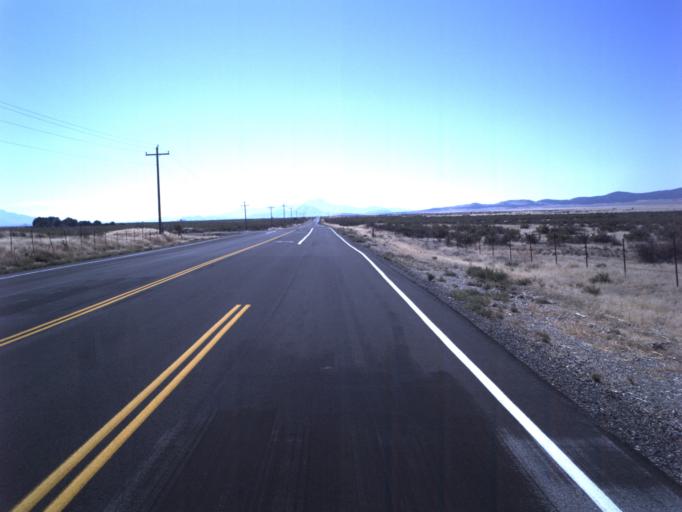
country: US
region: Utah
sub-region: Tooele County
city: Grantsville
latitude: 40.3557
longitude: -112.7457
